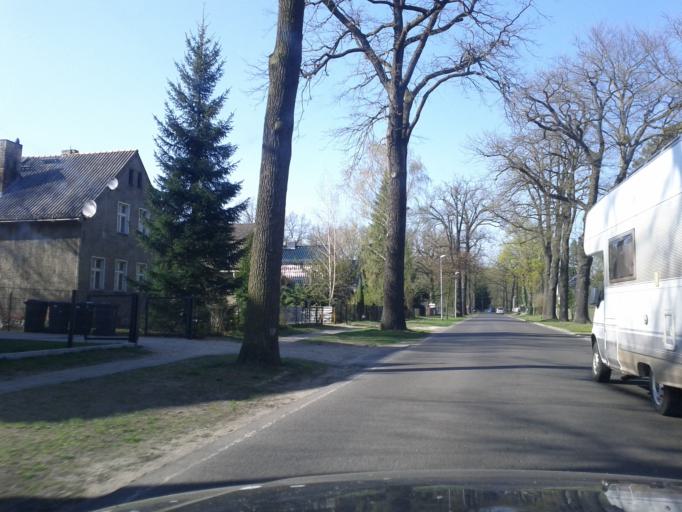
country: DE
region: Brandenburg
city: Schoneiche
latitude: 52.4733
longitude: 13.6938
